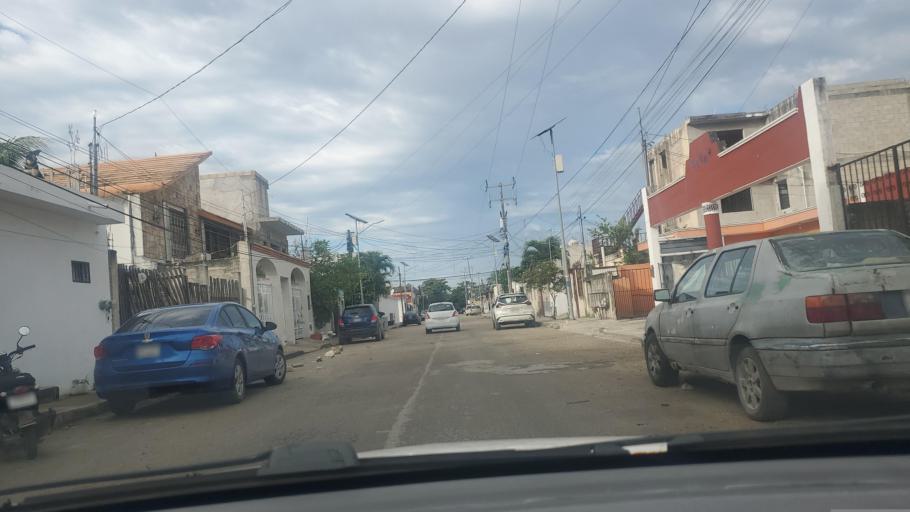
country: MX
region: Quintana Roo
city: Tulum
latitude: 20.2134
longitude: -87.4604
